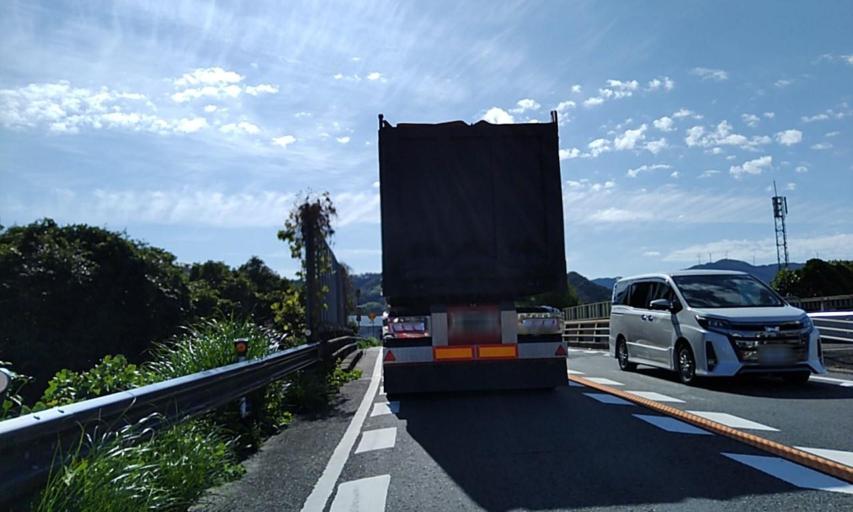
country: JP
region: Wakayama
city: Kainan
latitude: 34.0366
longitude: 135.1851
